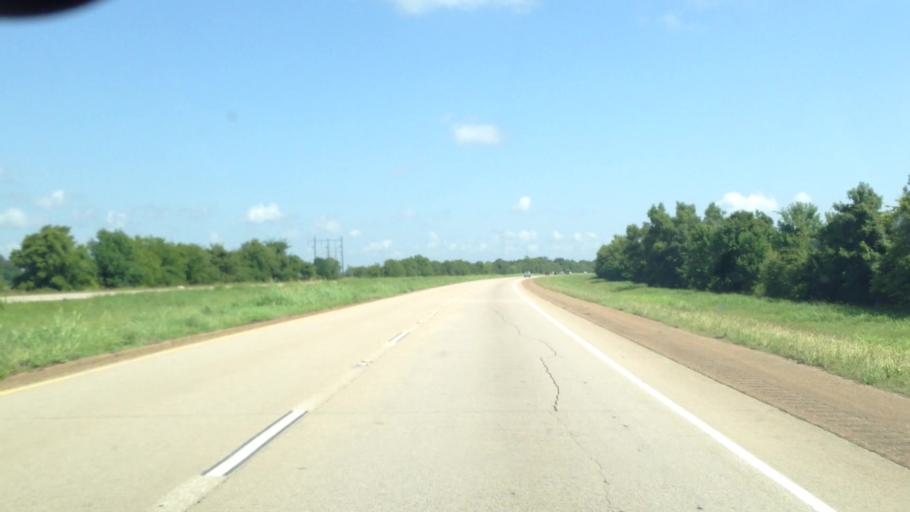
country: US
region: Louisiana
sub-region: Rapides Parish
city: Woodworth
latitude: 31.1876
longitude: -92.4722
